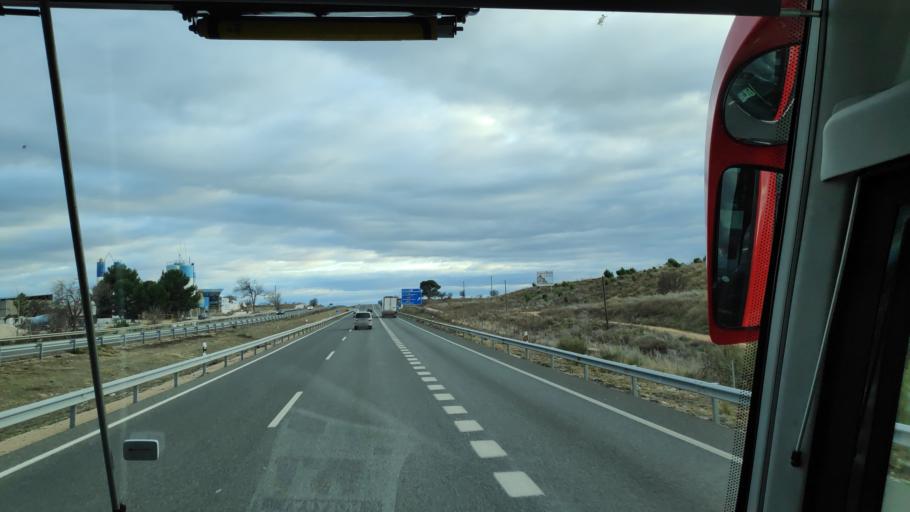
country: ES
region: Madrid
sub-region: Provincia de Madrid
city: Villarejo de Salvanes
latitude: 40.1859
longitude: -3.2982
